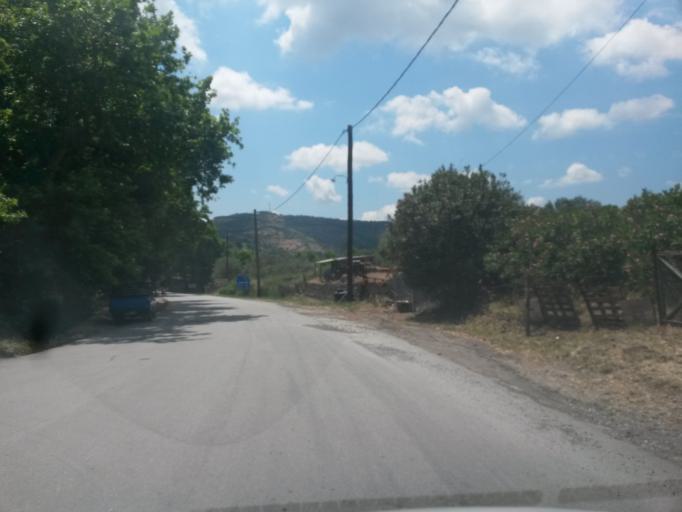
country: GR
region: North Aegean
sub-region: Nomos Lesvou
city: Eresos
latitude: 39.2265
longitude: 26.0490
